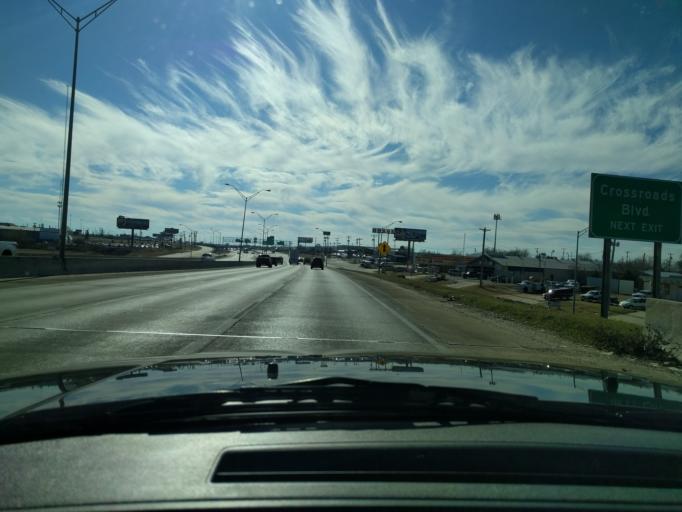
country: US
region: Oklahoma
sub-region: Oklahoma County
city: Del City
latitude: 35.4060
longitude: -97.4942
